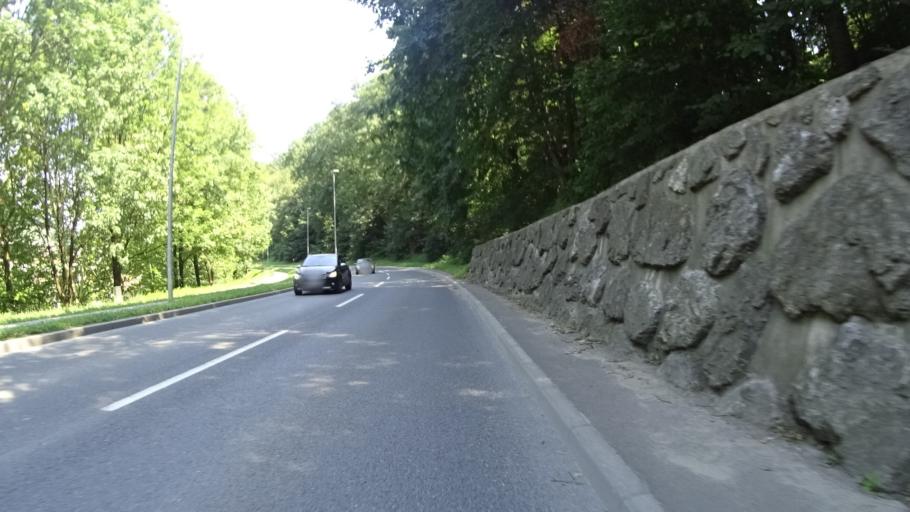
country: SI
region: Ravne na Koroskem
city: Ravne na Koroskem
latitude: 46.5424
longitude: 14.9555
